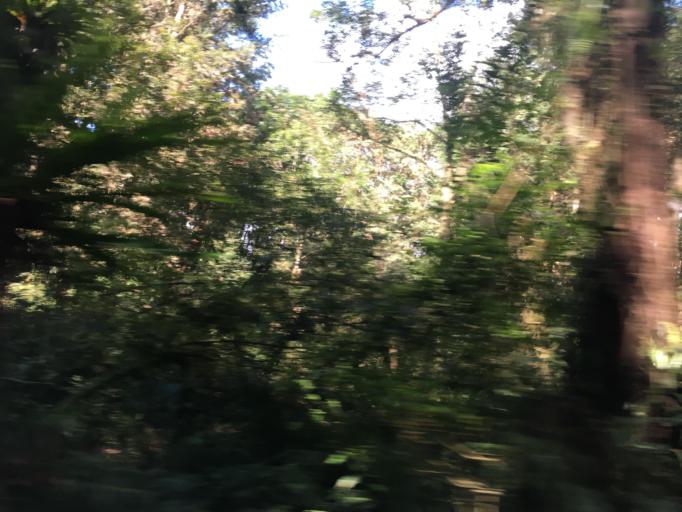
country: TW
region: Taiwan
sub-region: Yilan
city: Yilan
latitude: 24.7571
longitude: 121.5930
